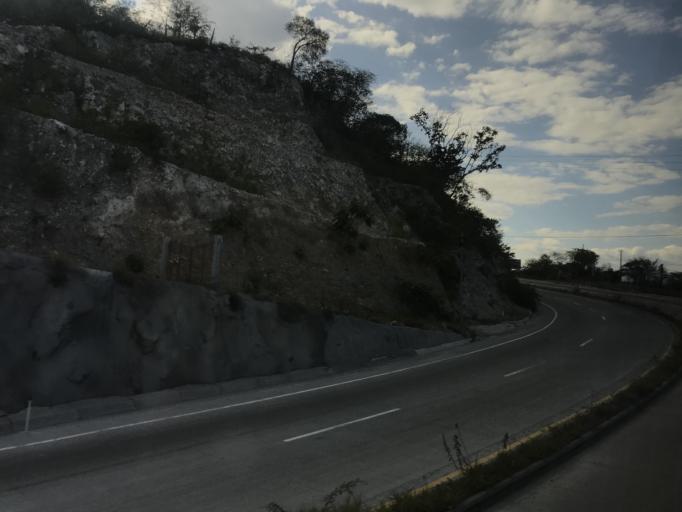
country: GT
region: El Progreso
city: Guastatoya
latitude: 14.8509
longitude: -90.1053
